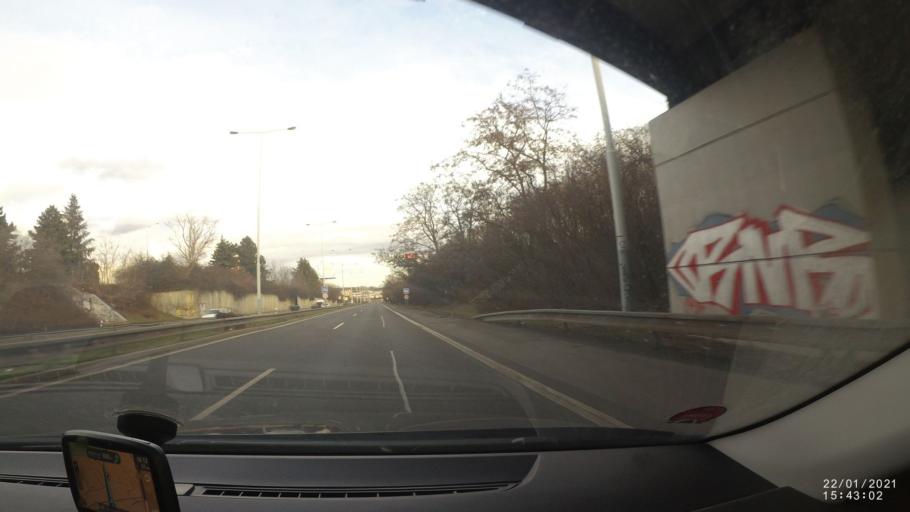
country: CZ
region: Central Bohemia
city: Hostivice
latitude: 50.0553
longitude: 14.3298
